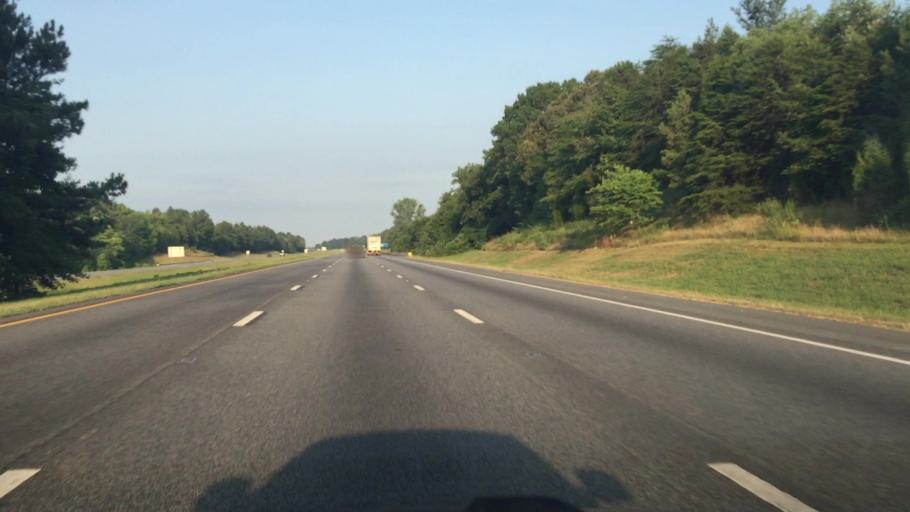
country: US
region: North Carolina
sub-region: Davidson County
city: Lexington
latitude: 35.8015
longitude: -80.1998
